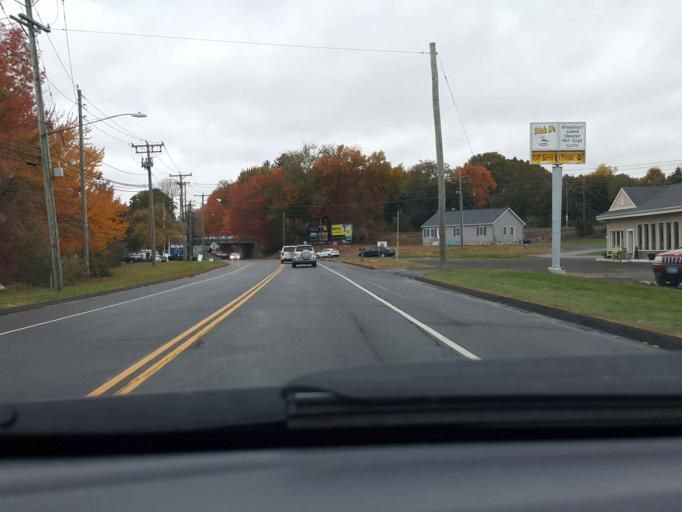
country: US
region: Connecticut
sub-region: New Haven County
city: Madison Center
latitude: 41.2820
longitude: -72.6316
